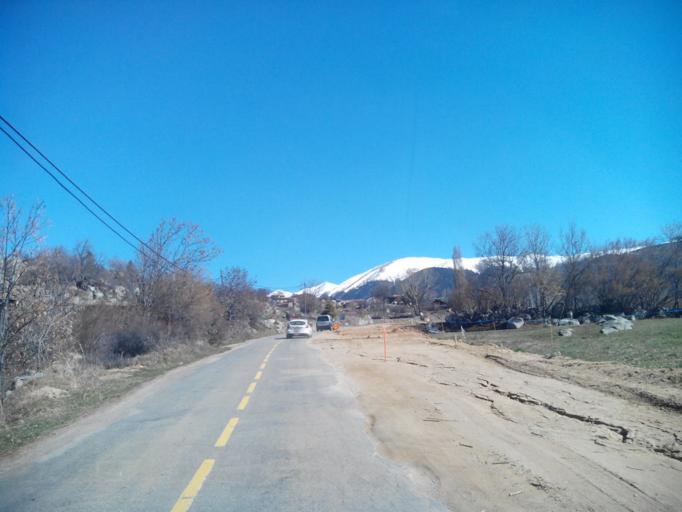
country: ES
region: Catalonia
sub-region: Provincia de Lleida
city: Lles de Cerdanya
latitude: 42.3860
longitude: 1.6856
